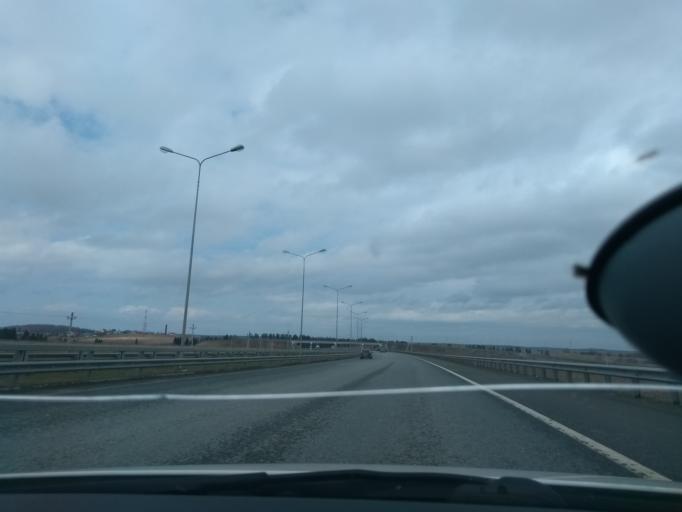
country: RU
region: Perm
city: Zvezdnyy
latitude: 57.7775
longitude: 56.3389
